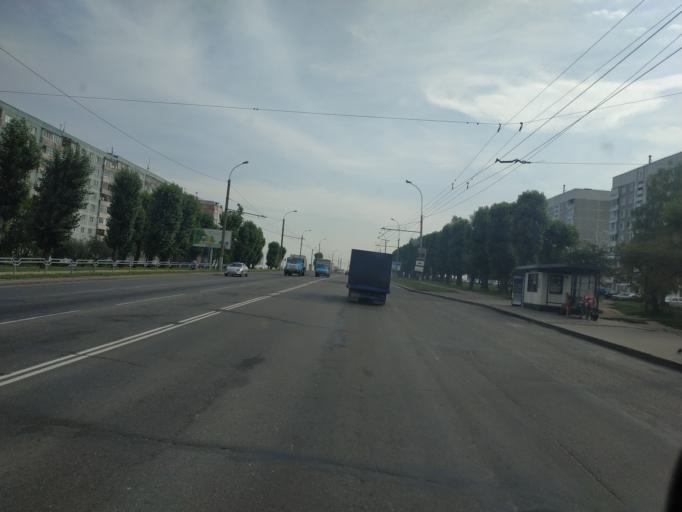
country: BY
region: Mogilev
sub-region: Mahilyowski Rayon
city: Veyno
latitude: 53.8757
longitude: 30.3783
